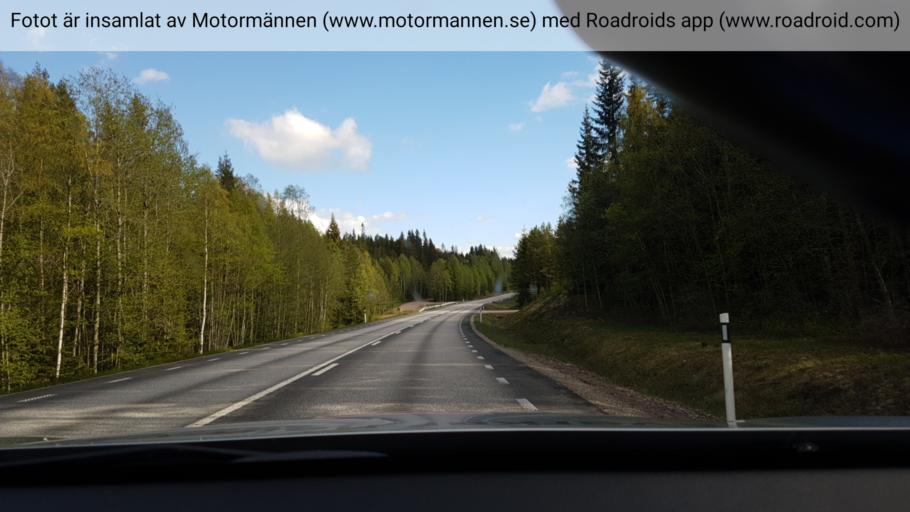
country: SE
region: Dalarna
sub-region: Faluns Kommun
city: Bjursas
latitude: 60.7810
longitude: 15.3130
